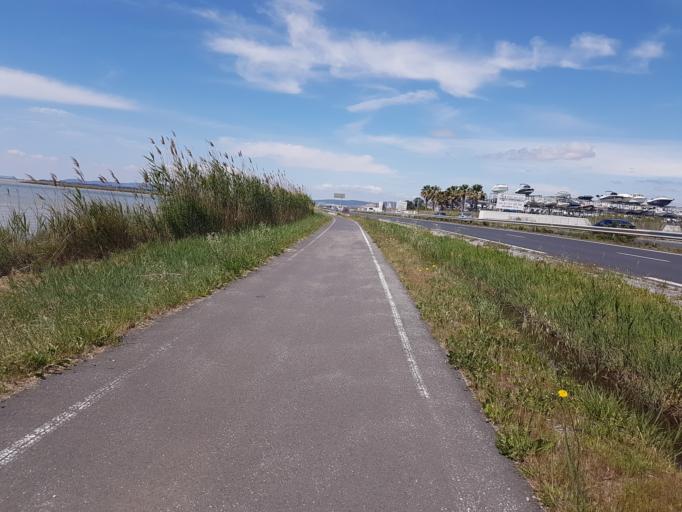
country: FR
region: Languedoc-Roussillon
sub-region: Departement de l'Herault
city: Palavas-les-Flots
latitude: 43.5347
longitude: 3.9118
